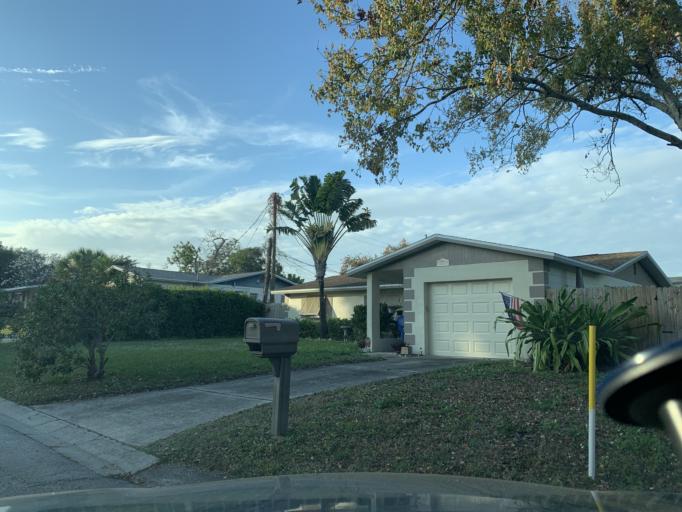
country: US
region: Florida
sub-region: Pinellas County
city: Ridgecrest
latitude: 27.8853
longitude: -82.7956
